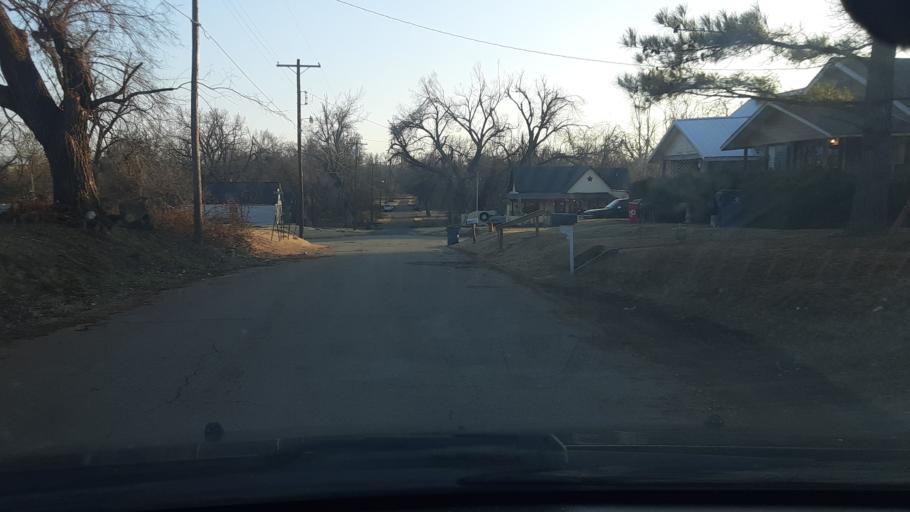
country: US
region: Oklahoma
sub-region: Logan County
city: Guthrie
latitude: 35.8754
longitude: -97.4288
